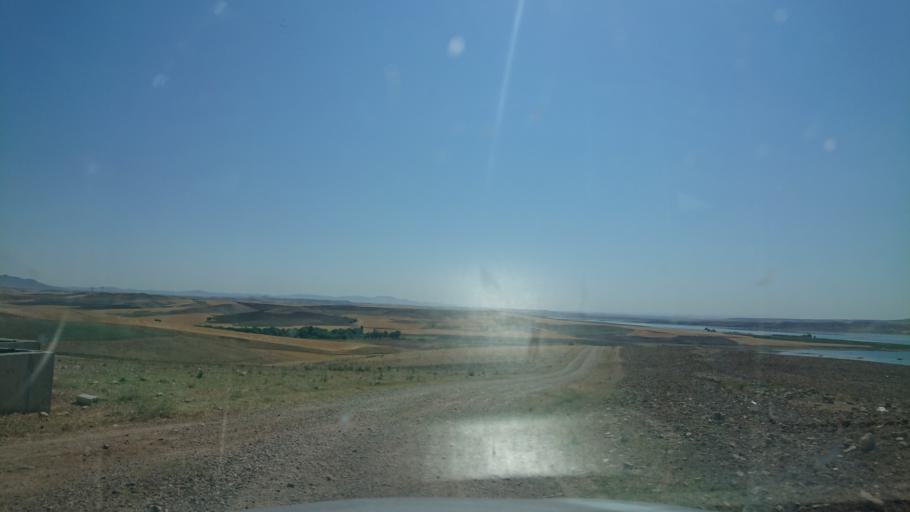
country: TR
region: Aksaray
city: Sariyahsi
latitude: 39.0563
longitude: 33.8889
